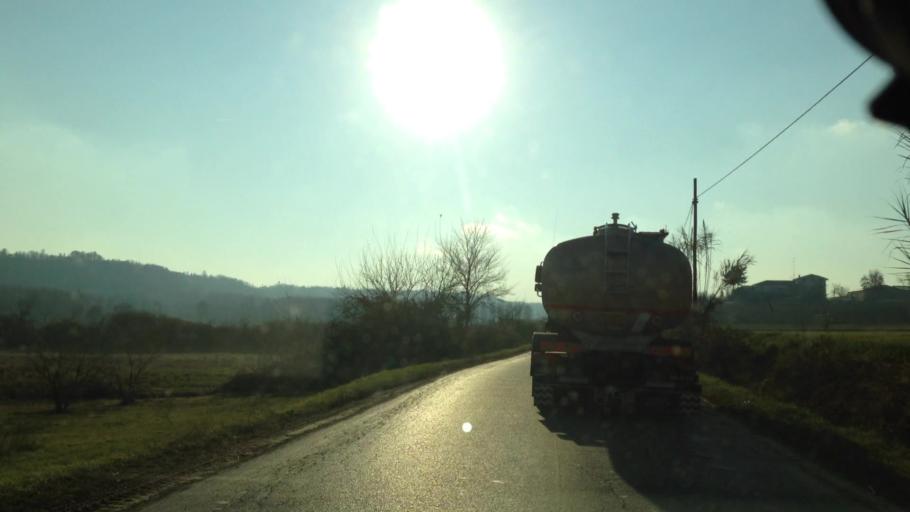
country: IT
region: Piedmont
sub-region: Provincia di Alessandria
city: Masio
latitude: 44.8494
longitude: 8.3997
